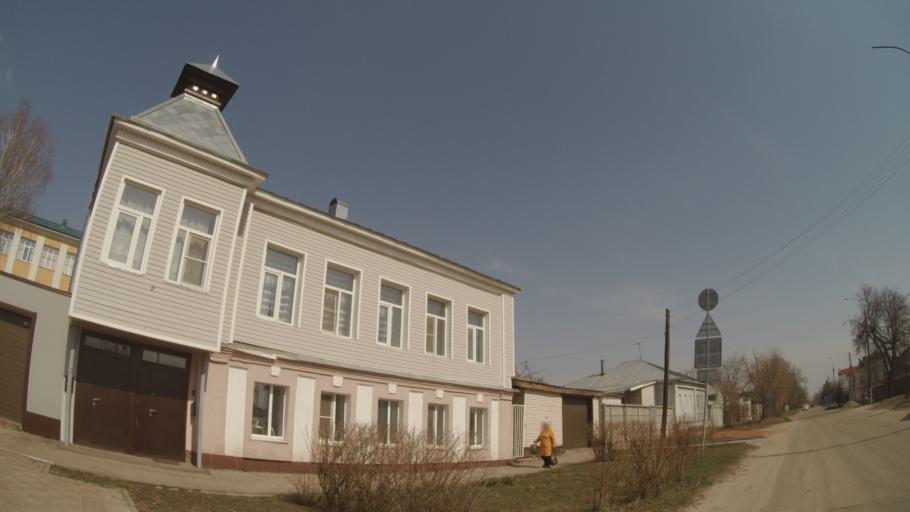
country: RU
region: Nizjnij Novgorod
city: Arzamas
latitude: 55.3851
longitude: 43.8214
